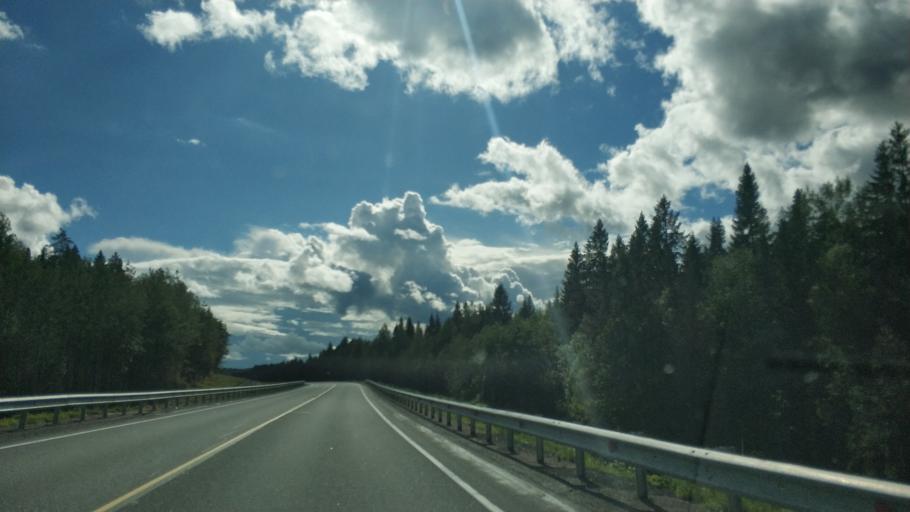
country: RU
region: Republic of Karelia
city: Ruskeala
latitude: 61.8638
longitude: 30.6531
